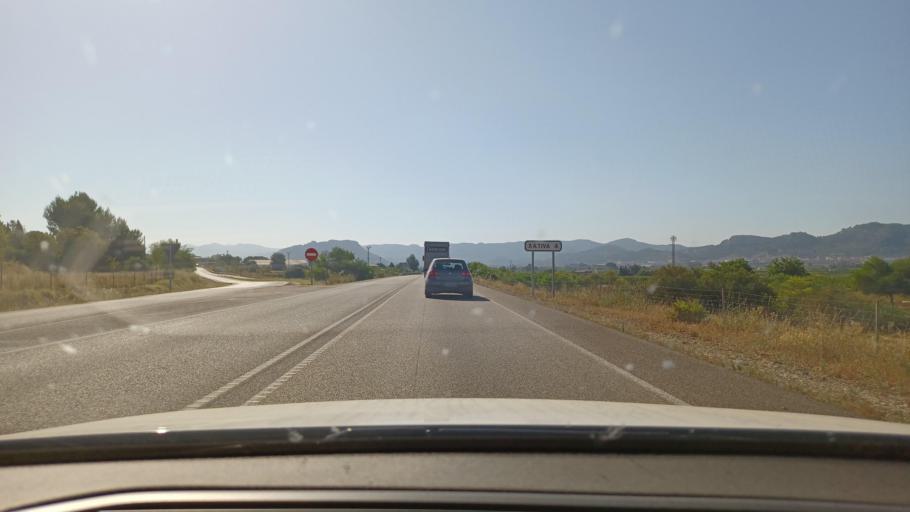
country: ES
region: Valencia
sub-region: Provincia de Valencia
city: Llosa de Ranes
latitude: 39.0170
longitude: -0.5502
